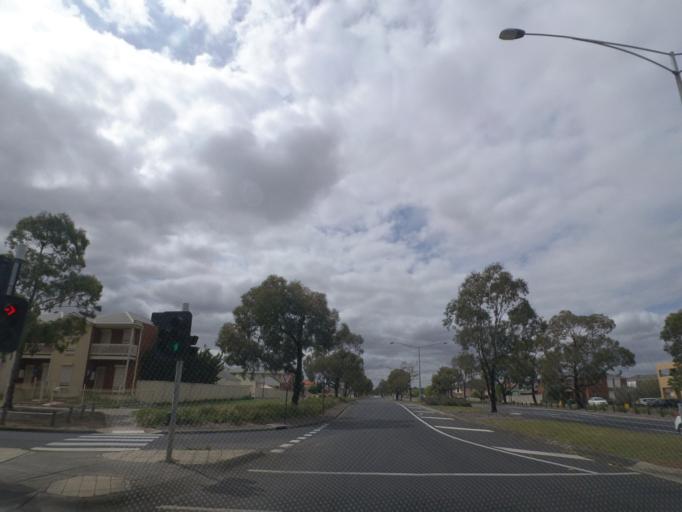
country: AU
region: Victoria
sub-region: Brimbank
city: Cairnlea
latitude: -37.7525
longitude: 144.7779
